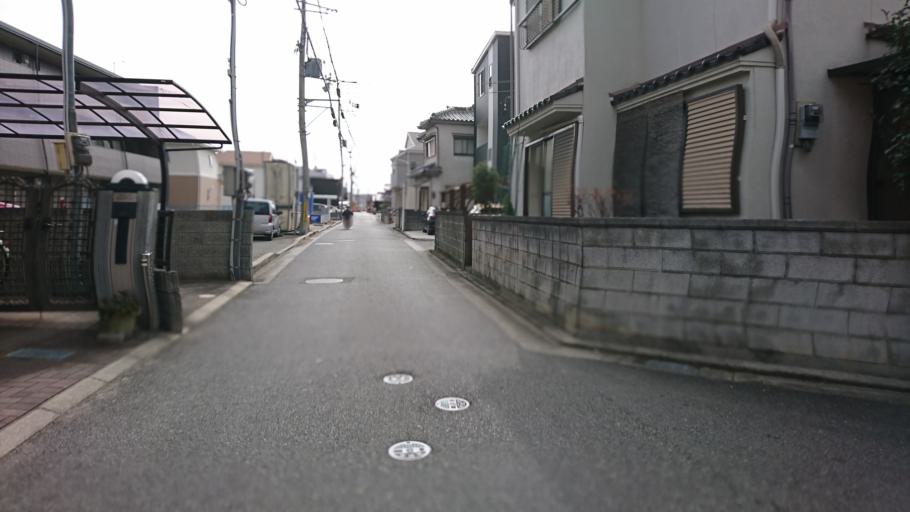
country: JP
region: Hyogo
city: Kakogawacho-honmachi
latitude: 34.7569
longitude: 134.8580
